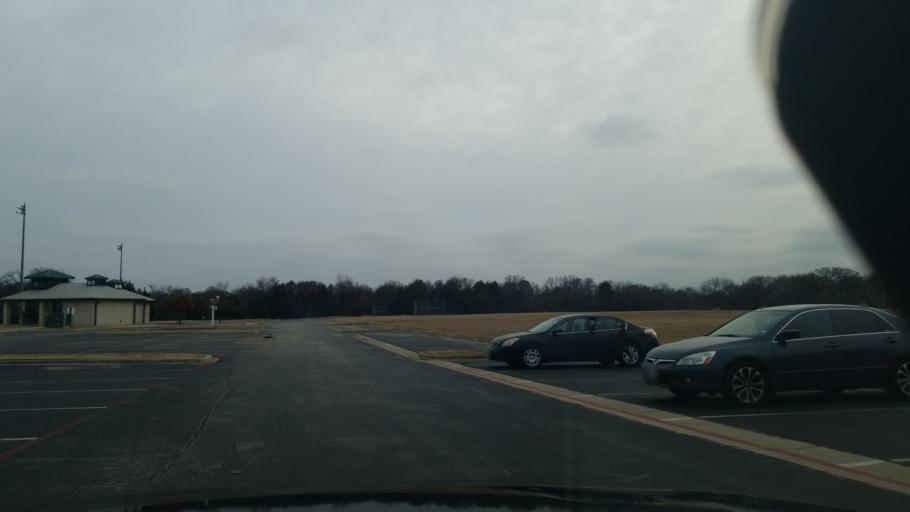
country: US
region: Texas
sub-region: Denton County
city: Corinth
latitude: 33.1531
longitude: -97.0507
